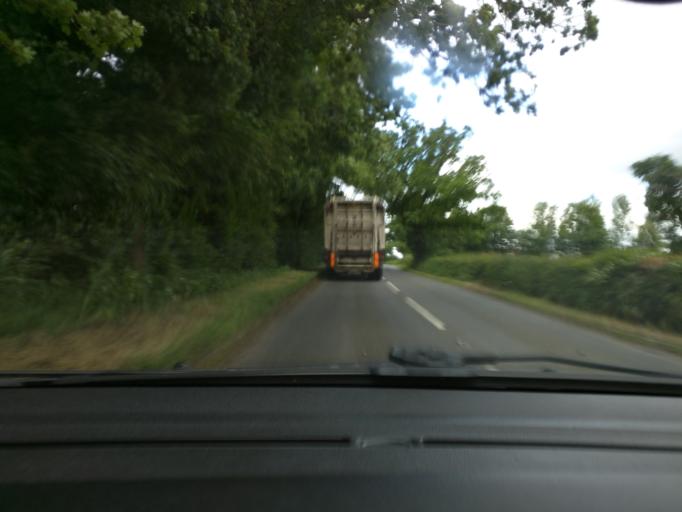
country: GB
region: England
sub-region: Suffolk
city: Saxmundham
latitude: 52.2275
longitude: 1.4603
